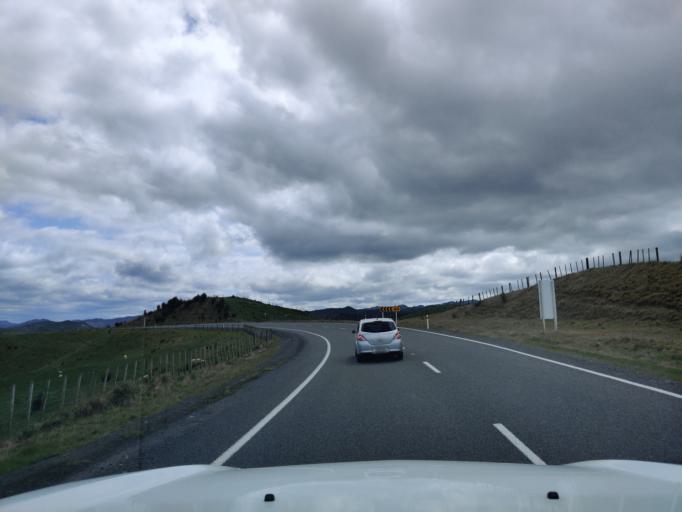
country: NZ
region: Manawatu-Wanganui
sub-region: Wanganui District
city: Wanganui
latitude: -39.7848
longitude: 175.2299
